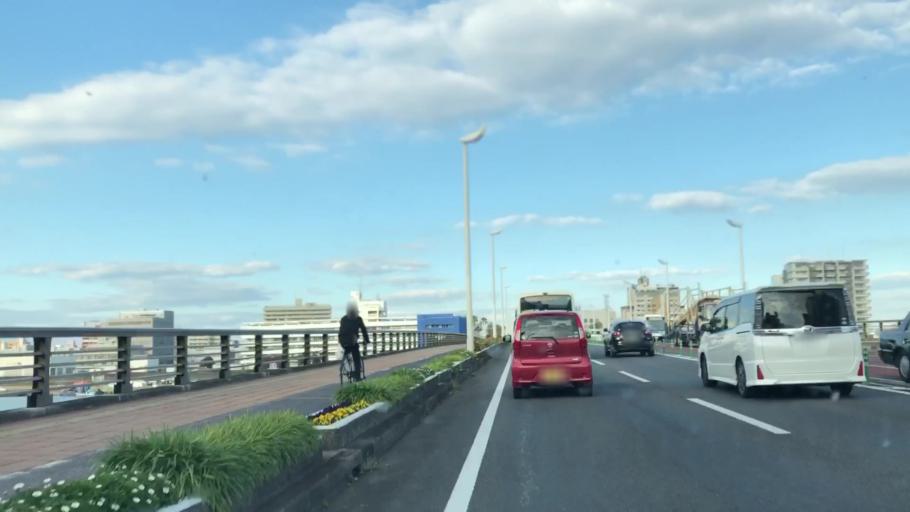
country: JP
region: Miyazaki
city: Miyazaki-shi
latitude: 31.9041
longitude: 131.4195
